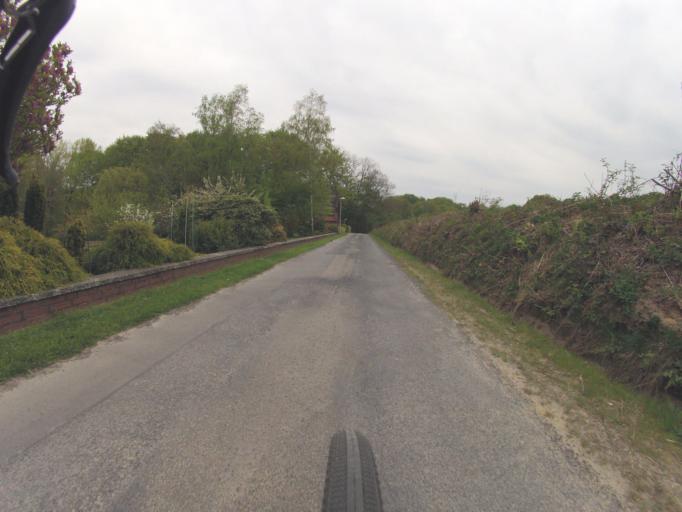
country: DE
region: North Rhine-Westphalia
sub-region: Regierungsbezirk Munster
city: Mettingen
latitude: 52.3079
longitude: 7.7888
